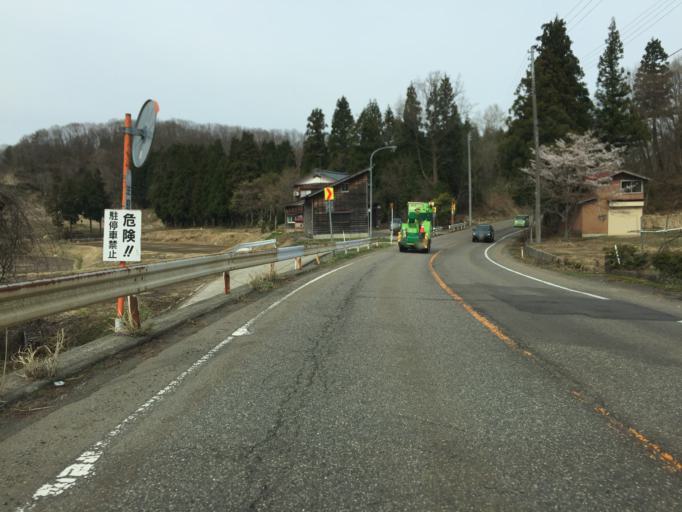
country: JP
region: Niigata
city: Tochio-honcho
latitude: 37.4613
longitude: 138.9730
